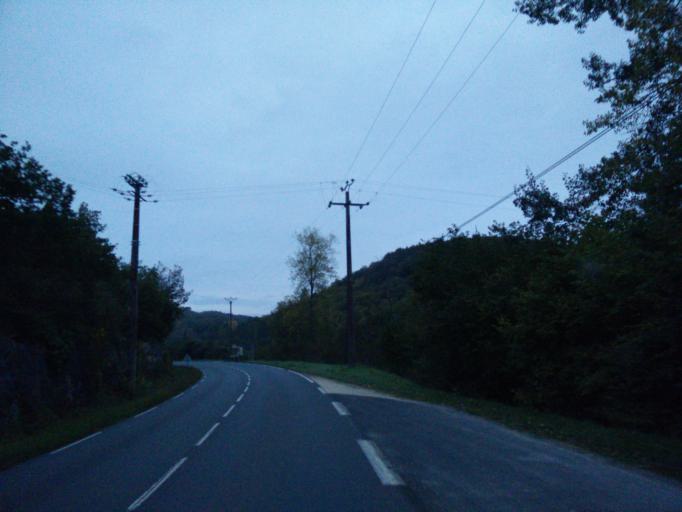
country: FR
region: Aquitaine
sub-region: Departement de la Dordogne
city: Saint-Cyprien
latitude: 44.9258
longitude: 1.0811
